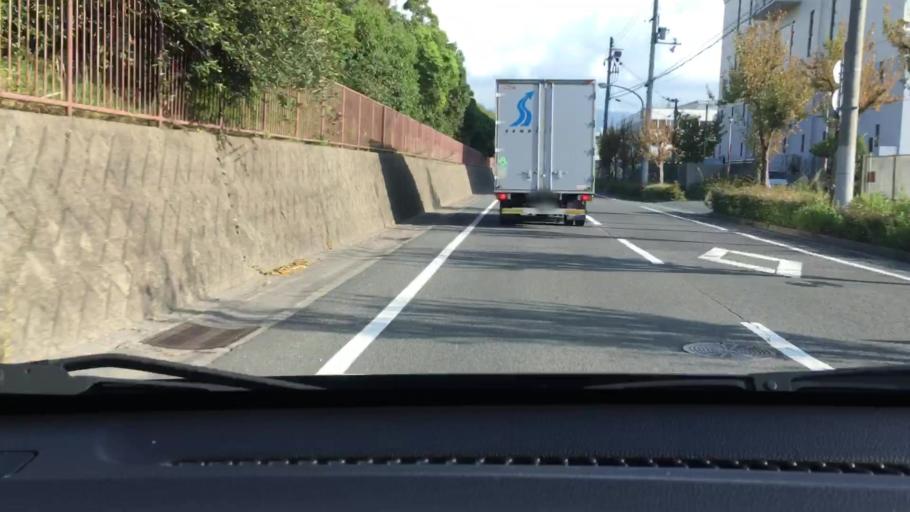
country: JP
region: Hyogo
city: Ashiya
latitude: 34.6885
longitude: 135.2758
